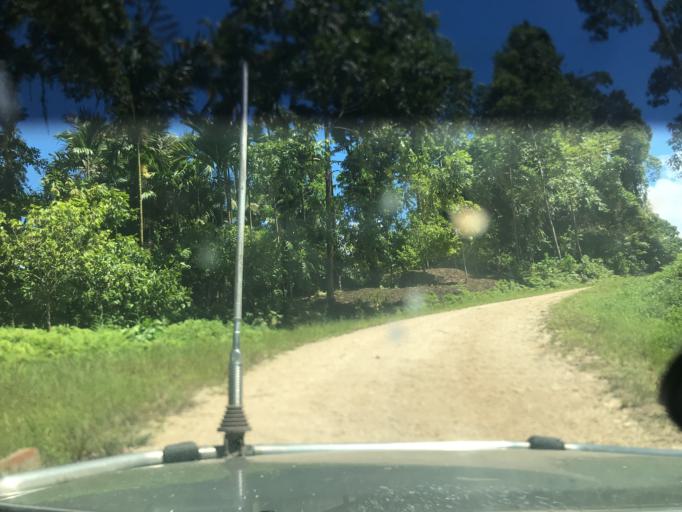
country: SB
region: Malaita
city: Auki
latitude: -8.7314
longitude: 160.9127
